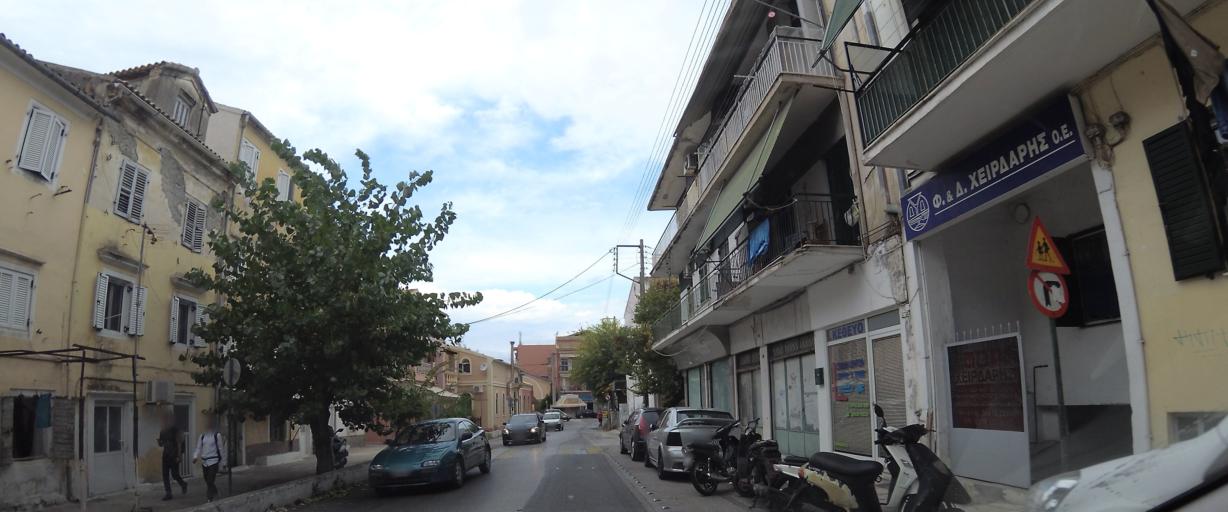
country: GR
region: Ionian Islands
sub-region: Nomos Kerkyras
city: Kerkyra
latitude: 39.6243
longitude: 19.9094
